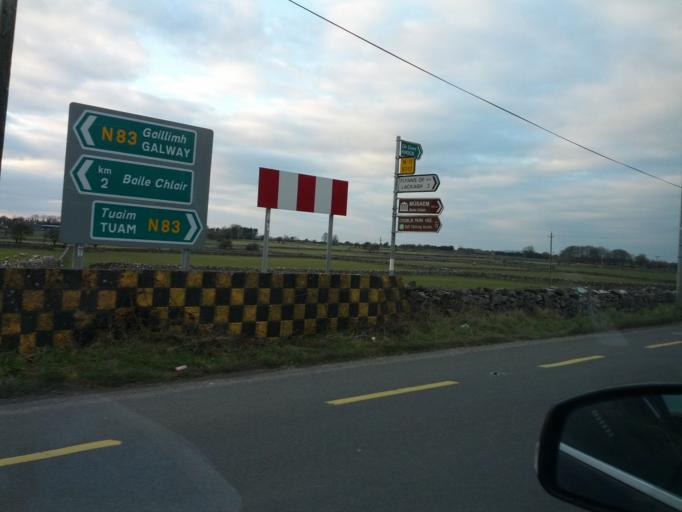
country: IE
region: Connaught
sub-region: County Galway
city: Claregalway
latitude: 53.3618
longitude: -8.9267
